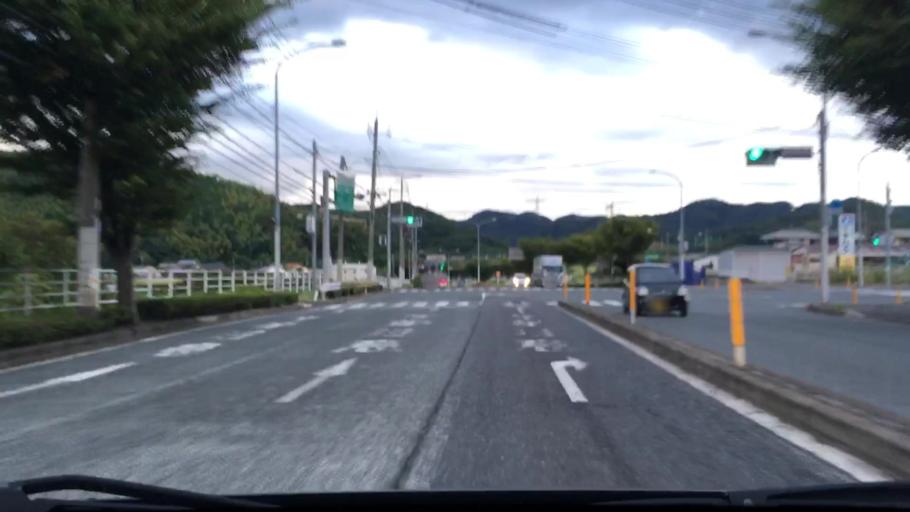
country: JP
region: Yamaguchi
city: Shimonoseki
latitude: 33.8874
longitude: 130.9780
